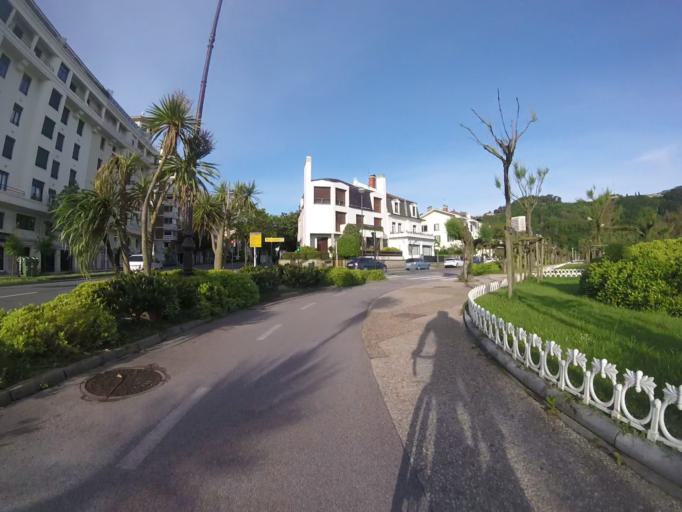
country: ES
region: Basque Country
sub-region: Provincia de Guipuzcoa
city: San Sebastian
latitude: 43.3154
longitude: -2.0012
